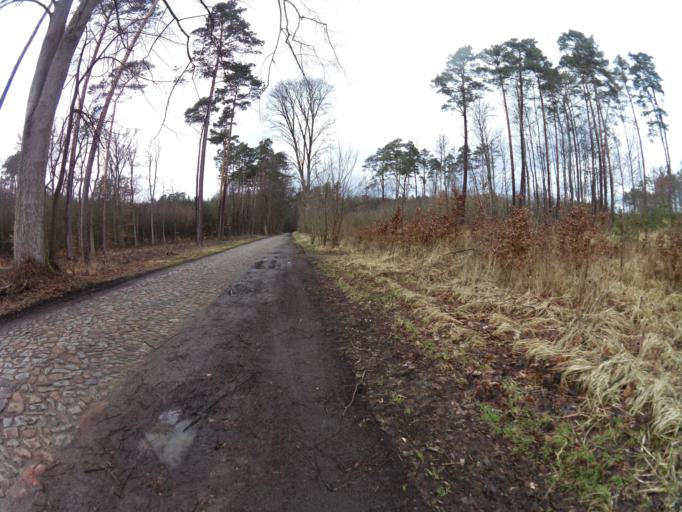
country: PL
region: West Pomeranian Voivodeship
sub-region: Powiat mysliborski
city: Debno
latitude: 52.7299
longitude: 14.7265
